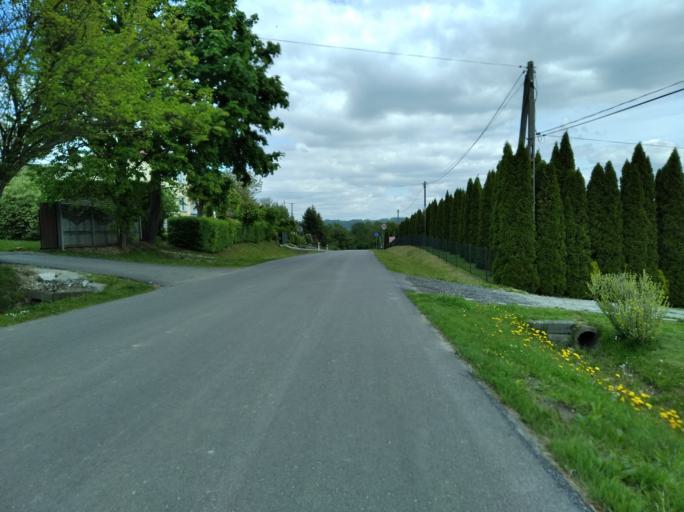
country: PL
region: Subcarpathian Voivodeship
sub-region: Powiat ropczycko-sedziszowski
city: Wielopole Skrzynskie
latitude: 49.9372
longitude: 21.6034
